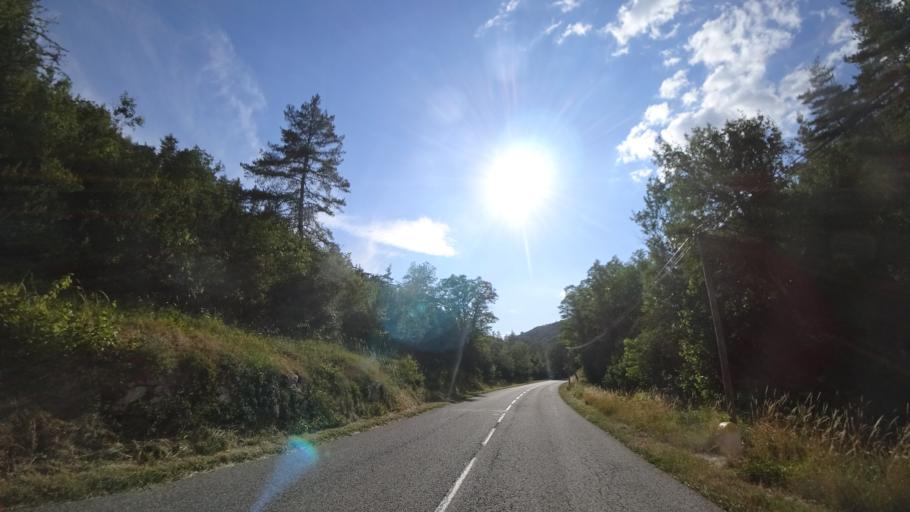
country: FR
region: Languedoc-Roussillon
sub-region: Departement de la Lozere
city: La Canourgue
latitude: 44.4108
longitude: 3.2697
